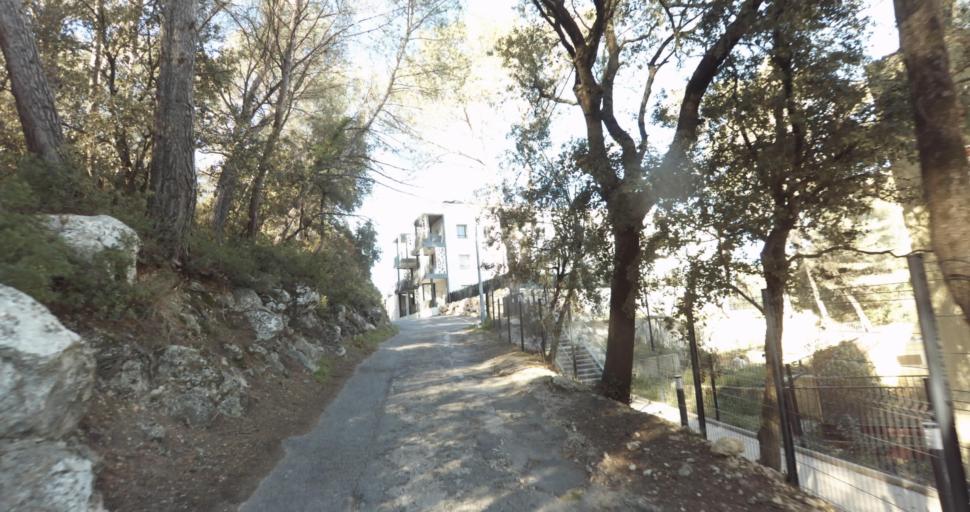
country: FR
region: Provence-Alpes-Cote d'Azur
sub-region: Departement des Bouches-du-Rhone
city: Peypin
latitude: 43.3840
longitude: 5.5826
